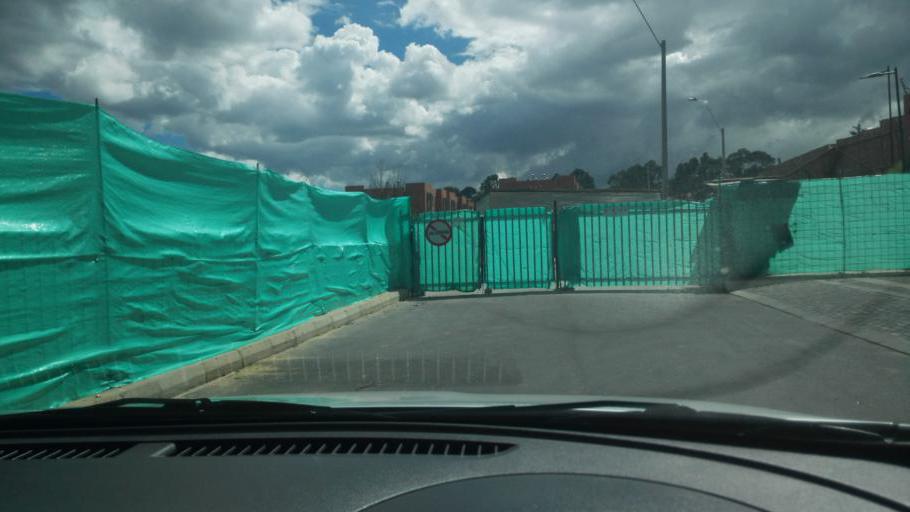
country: CO
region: Cundinamarca
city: Cota
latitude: 4.7407
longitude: -74.0705
